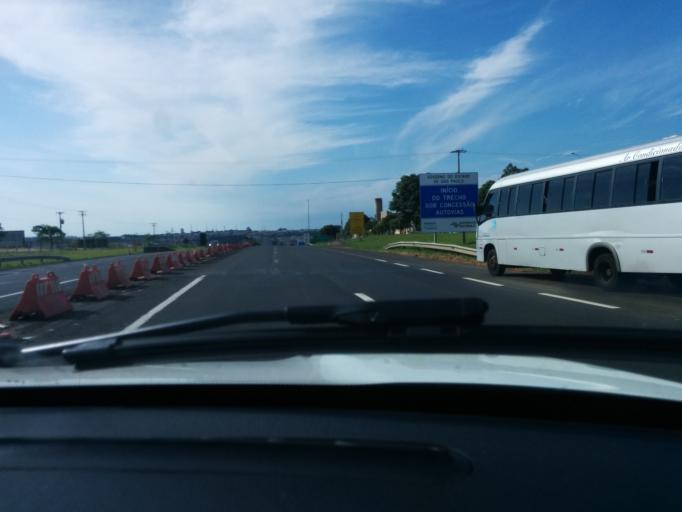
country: BR
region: Sao Paulo
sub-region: Franca
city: Franca
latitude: -20.4718
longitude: -47.4129
